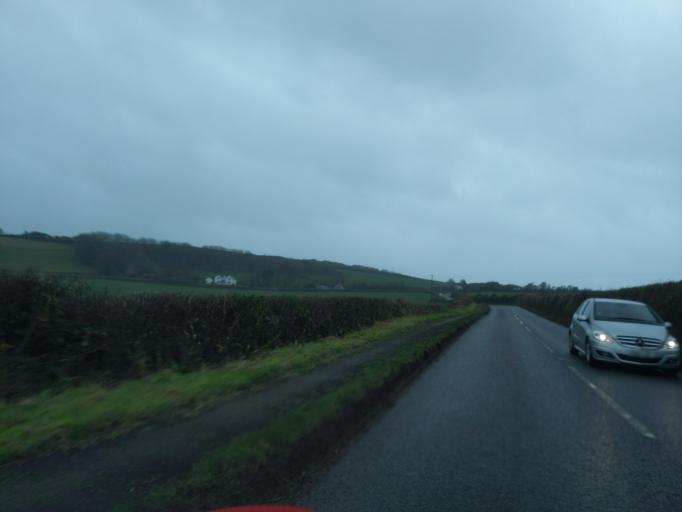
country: GB
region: England
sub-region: Cornwall
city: Saltash
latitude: 50.3641
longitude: -4.2625
